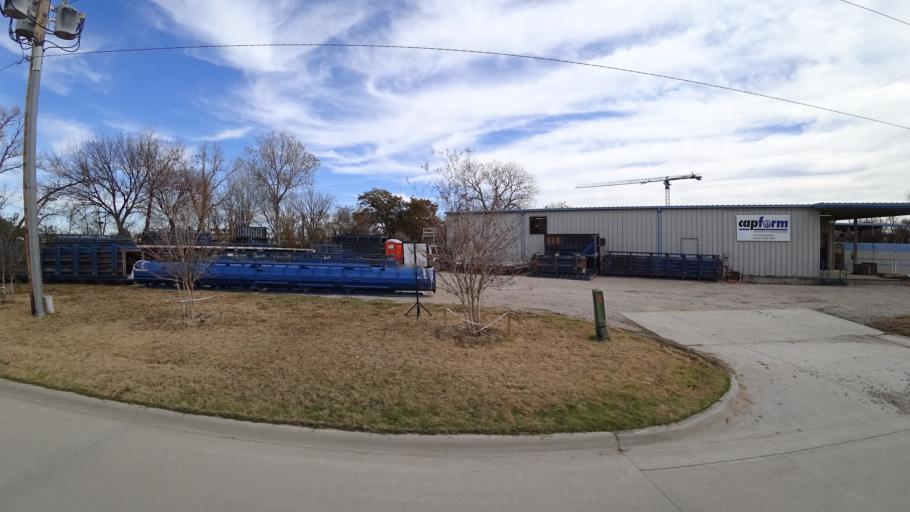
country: US
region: Texas
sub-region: Denton County
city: Lewisville
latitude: 33.0347
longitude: -96.9791
